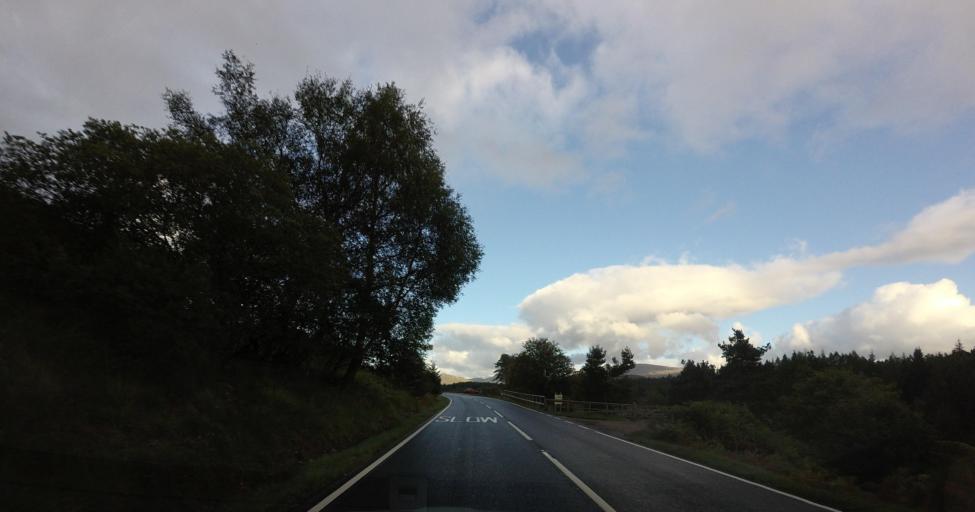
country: GB
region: Scotland
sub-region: Highland
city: Spean Bridge
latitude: 56.8905
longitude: -4.6762
